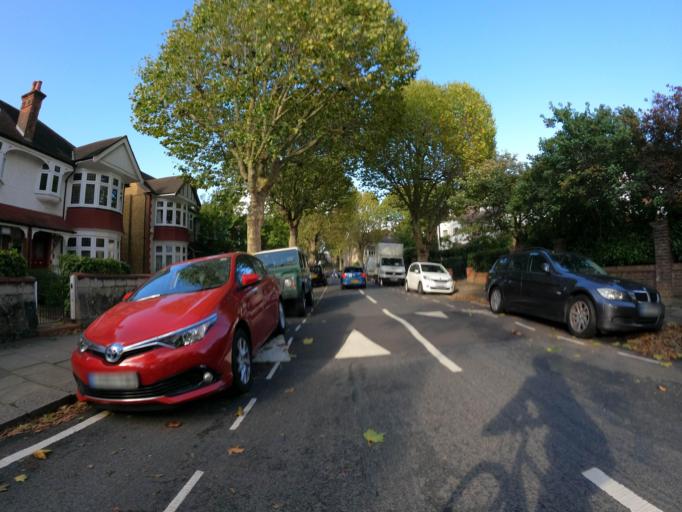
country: GB
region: England
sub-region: Greater London
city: Ealing
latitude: 51.5054
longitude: -0.2988
